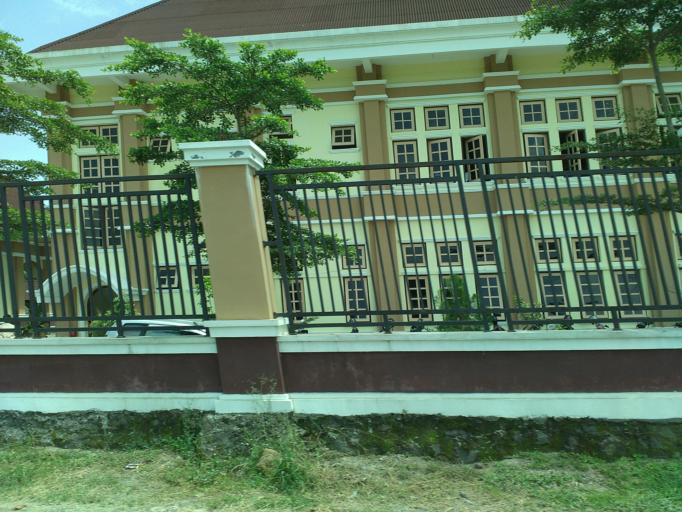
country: ID
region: Central Java
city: Klaten
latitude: -7.7036
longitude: 110.5958
